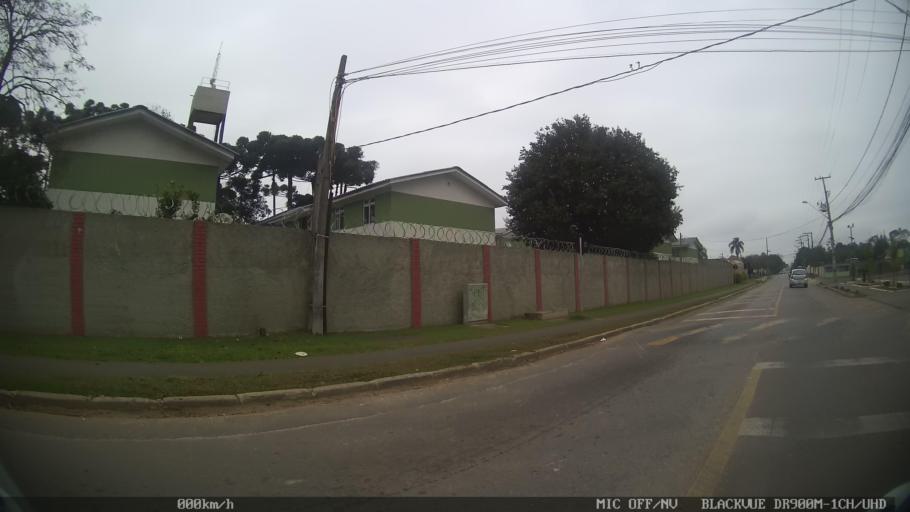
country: BR
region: Parana
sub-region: Almirante Tamandare
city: Almirante Tamandare
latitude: -25.3725
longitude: -49.3308
